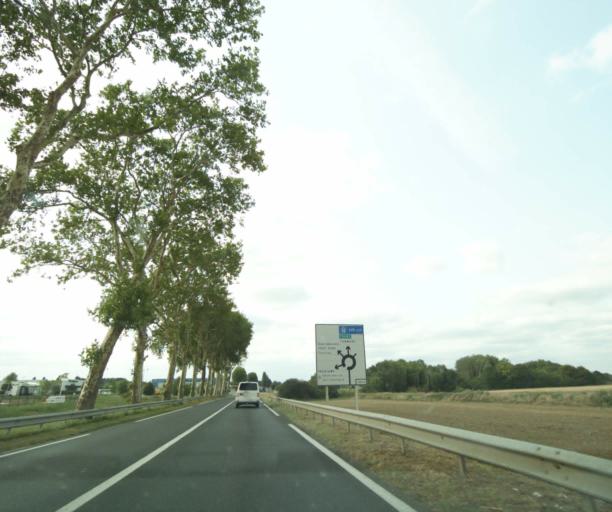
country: FR
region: Centre
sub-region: Departement d'Indre-et-Loire
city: Cormery
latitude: 47.2557
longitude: 0.8442
